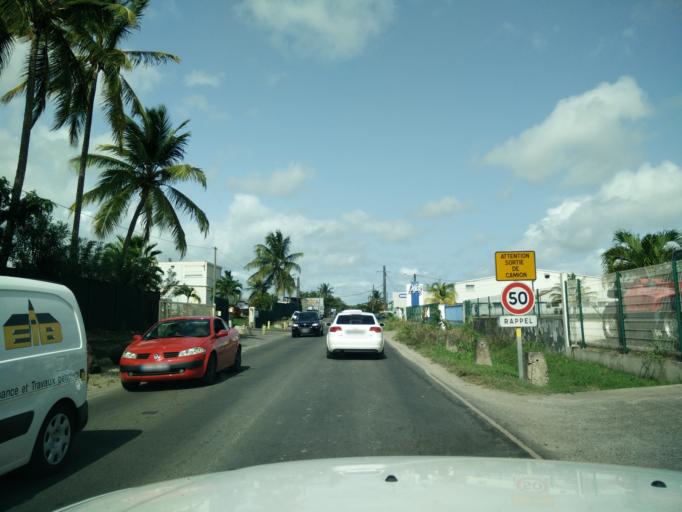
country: GP
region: Guadeloupe
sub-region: Guadeloupe
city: Pointe-a-Pitre
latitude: 16.2459
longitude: -61.5589
